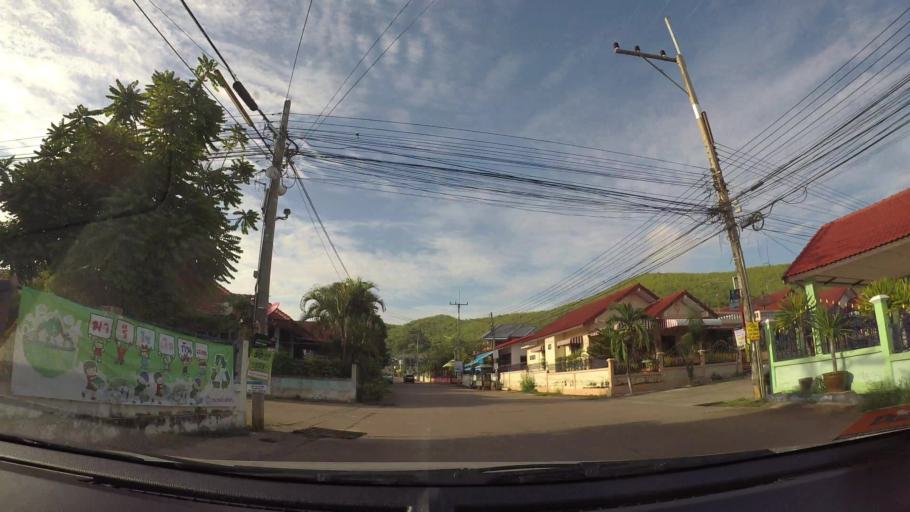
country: TH
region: Chon Buri
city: Sattahip
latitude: 12.6703
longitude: 100.9181
